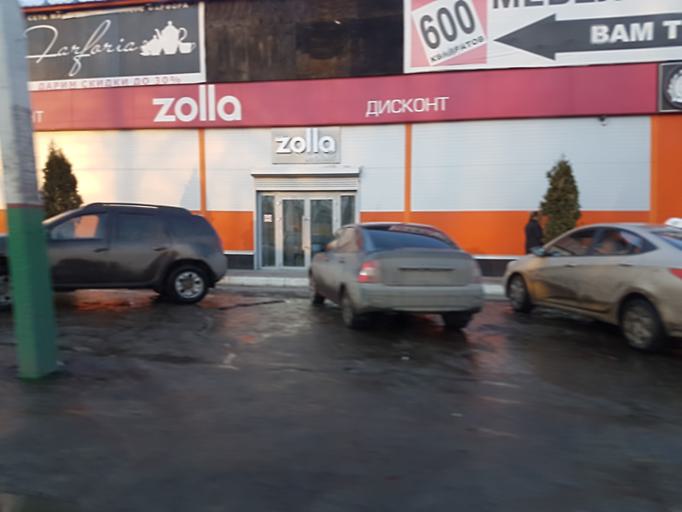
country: RU
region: Tambov
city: Michurinsk
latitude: 52.8992
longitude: 40.4845
